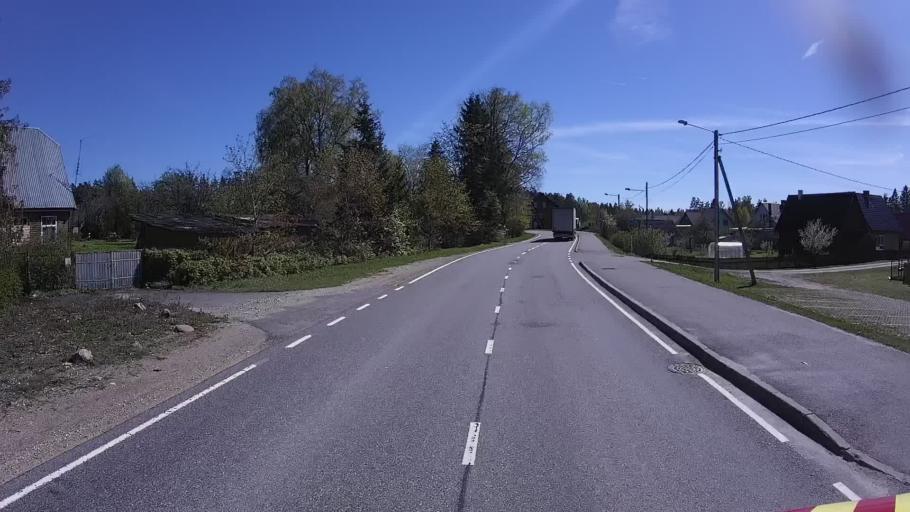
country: EE
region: Harju
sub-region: Kuusalu vald
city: Kuusalu
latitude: 59.2835
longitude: 25.6132
